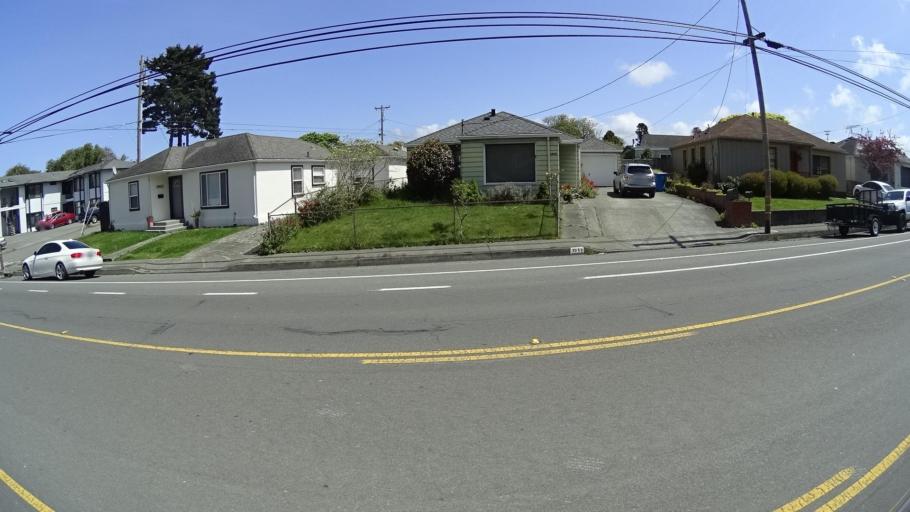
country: US
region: California
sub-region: Humboldt County
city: Myrtletown
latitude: 40.7907
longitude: -124.1339
